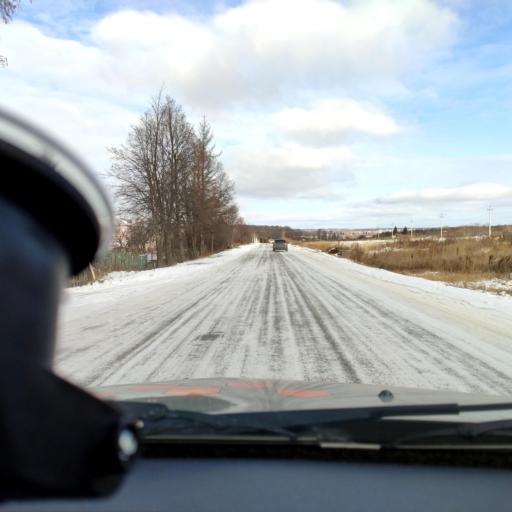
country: RU
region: Bashkortostan
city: Avdon
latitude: 54.7853
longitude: 55.7597
